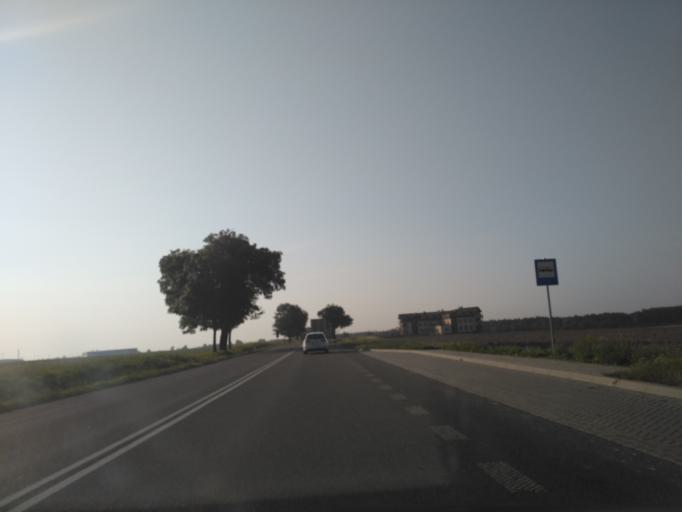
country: PL
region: Lublin Voivodeship
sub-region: Powiat janowski
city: Modliborzyce
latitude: 50.7297
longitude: 22.3608
